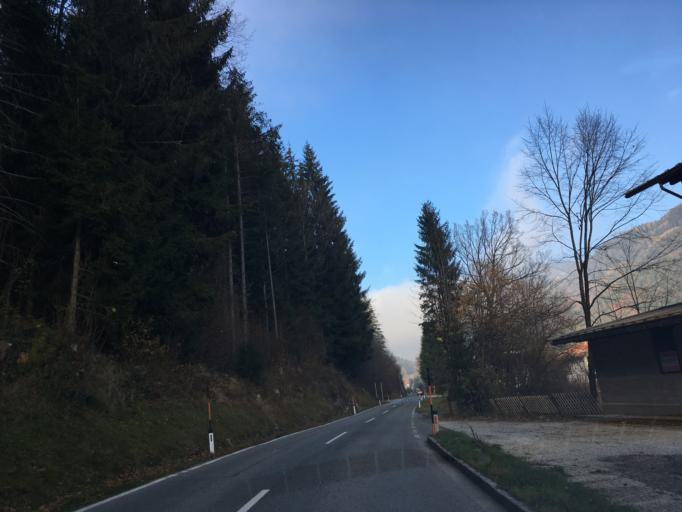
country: AT
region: Tyrol
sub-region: Politischer Bezirk Kufstein
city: Rettenschoss
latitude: 47.6752
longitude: 12.2530
